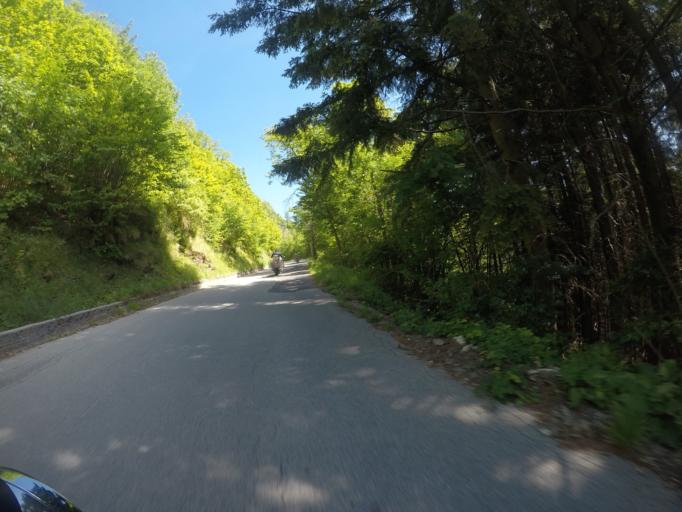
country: IT
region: Tuscany
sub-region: Provincia di Lucca
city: Careggine
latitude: 44.0973
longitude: 10.3271
